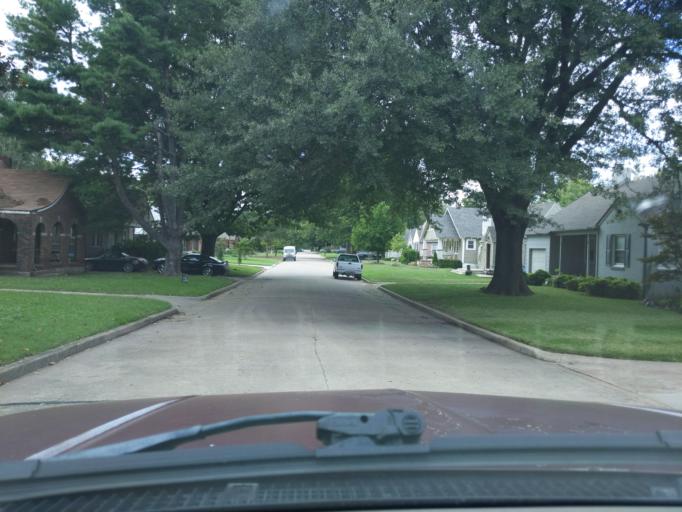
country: US
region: Oklahoma
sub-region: Tulsa County
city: Tulsa
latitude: 36.1107
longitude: -95.9787
